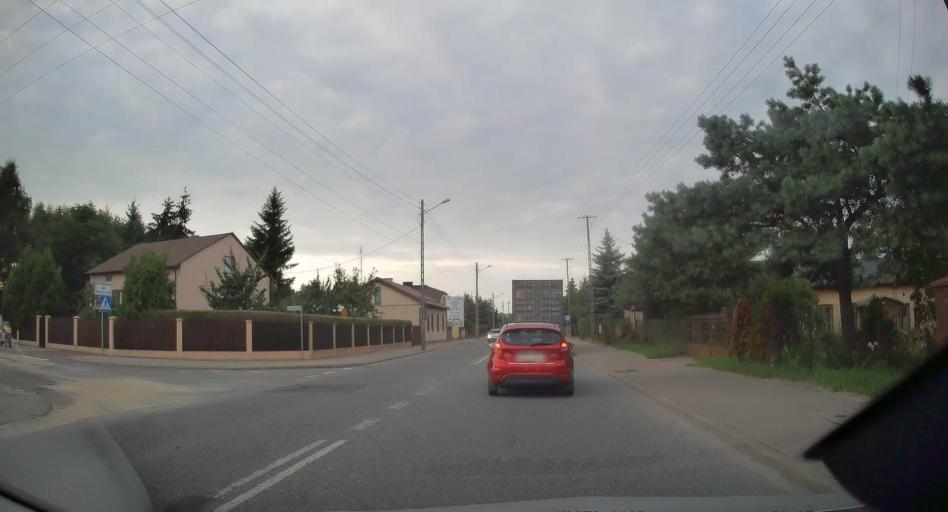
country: PL
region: Lodz Voivodeship
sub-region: Powiat radomszczanski
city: Kamiensk
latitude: 51.1967
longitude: 19.4991
